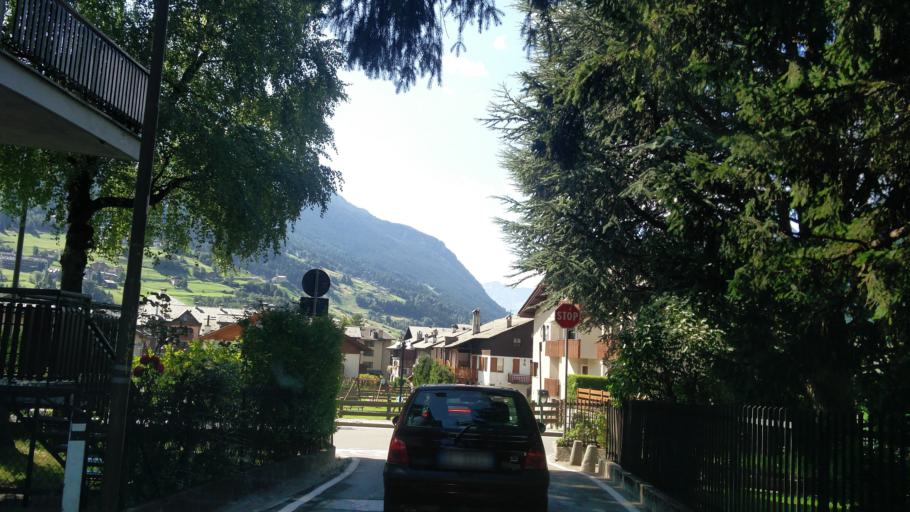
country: IT
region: Lombardy
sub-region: Provincia di Sondrio
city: Bormio
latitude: 46.4680
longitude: 10.3684
